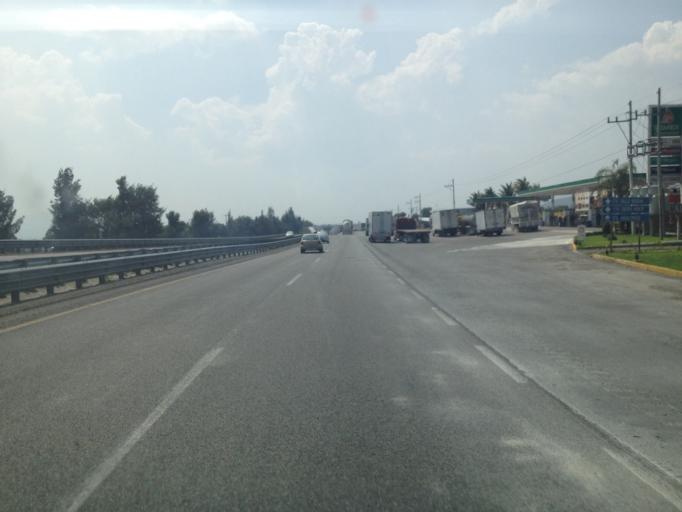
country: MX
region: Puebla
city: Cuacnopalan
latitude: 18.8289
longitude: -97.5037
